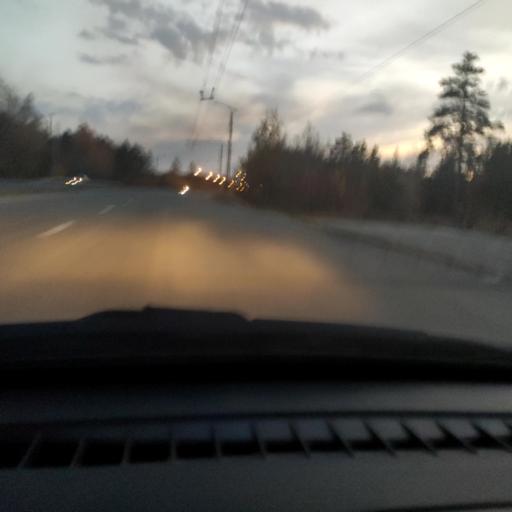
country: RU
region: Samara
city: Zhigulevsk
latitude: 53.5313
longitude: 49.5544
